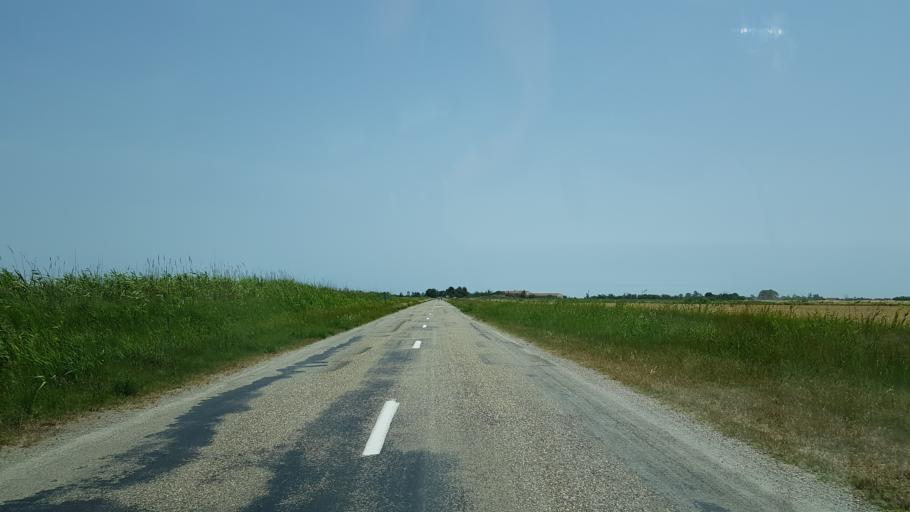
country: FR
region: Provence-Alpes-Cote d'Azur
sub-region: Departement des Bouches-du-Rhone
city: Port-Saint-Louis-du-Rhone
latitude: 43.4363
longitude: 4.6832
